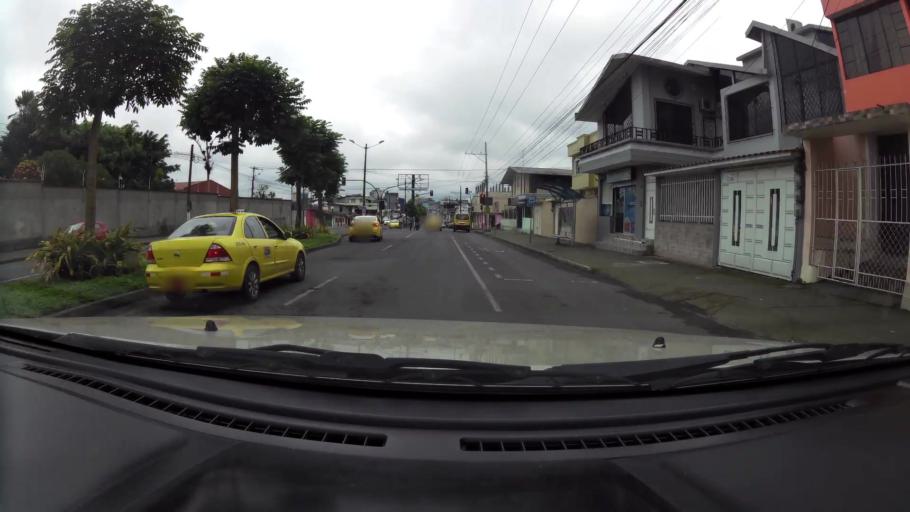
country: EC
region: Santo Domingo de los Tsachilas
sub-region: Canton Santo Domingo de los Colorados
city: Santo Domingo de los Colorados
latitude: -0.2570
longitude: -79.1611
